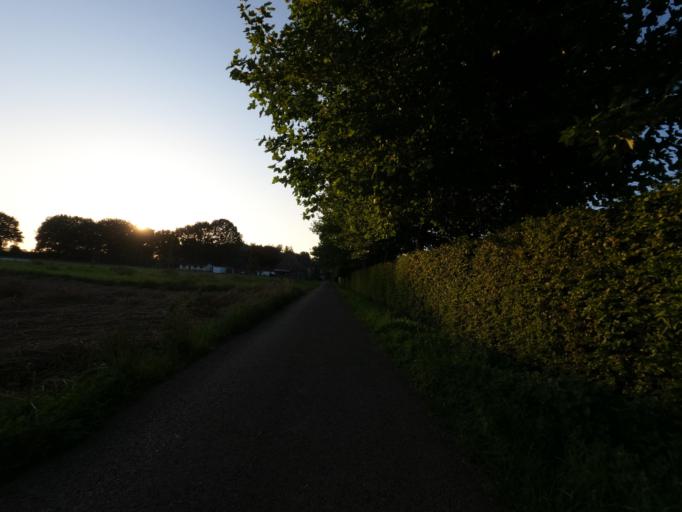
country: DE
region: North Rhine-Westphalia
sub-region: Regierungsbezirk Koln
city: Linnich
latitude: 51.0087
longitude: 6.2724
